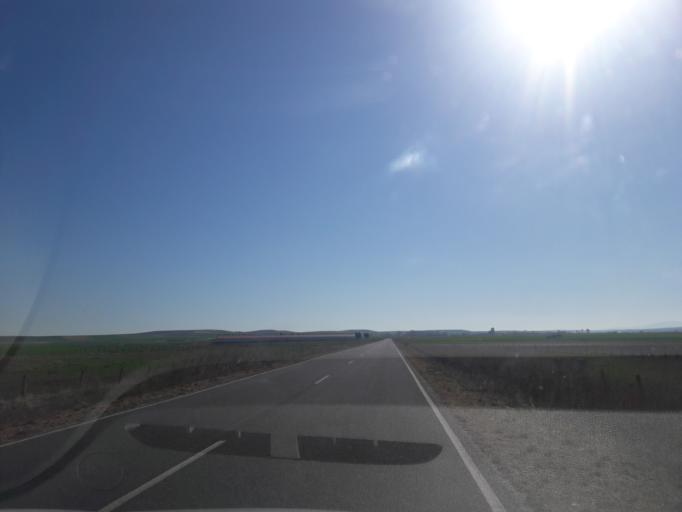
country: ES
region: Castille and Leon
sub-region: Provincia de Salamanca
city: Salmoral
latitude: 40.8100
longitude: -5.2467
